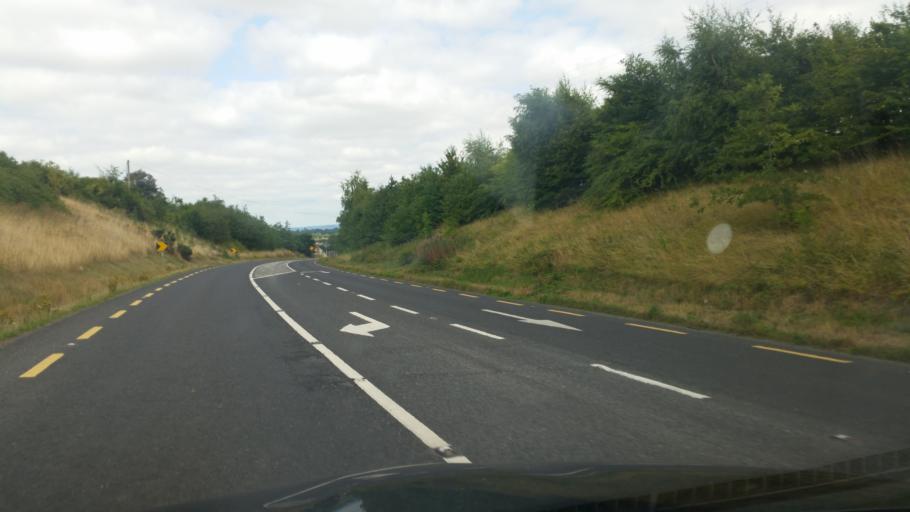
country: IE
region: Leinster
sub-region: County Carlow
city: Tullow
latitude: 52.7893
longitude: -6.7548
